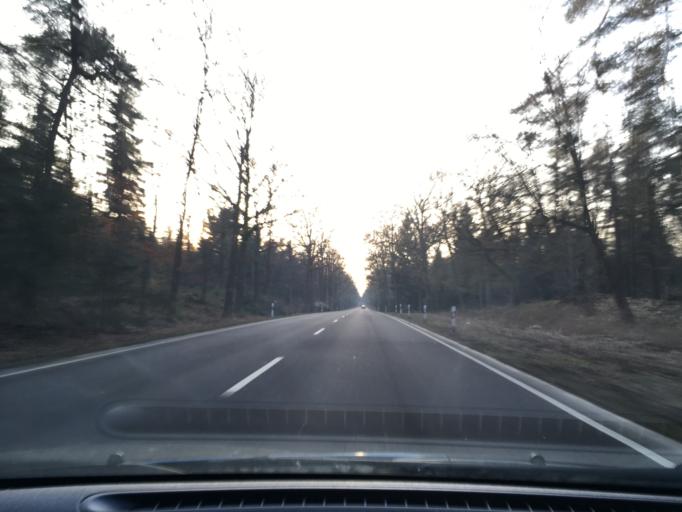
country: DE
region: Lower Saxony
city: Sprakensehl
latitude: 52.8215
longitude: 10.4552
